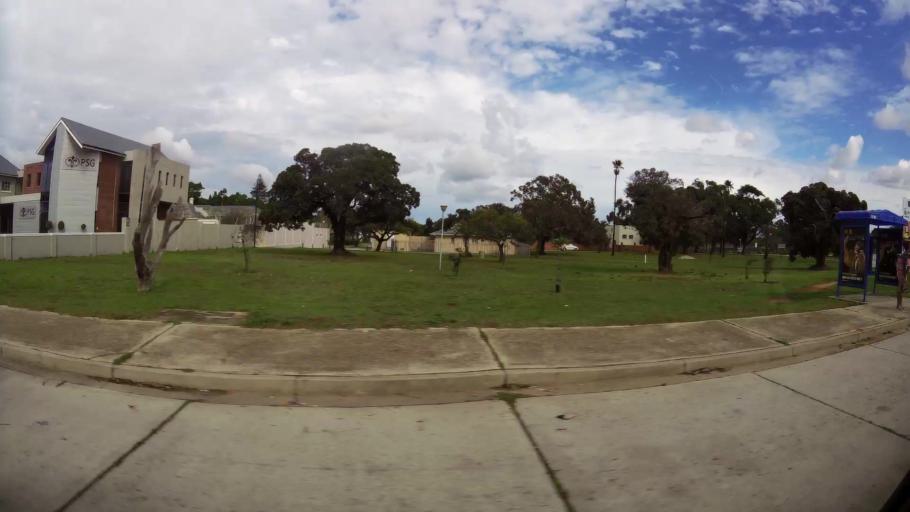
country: ZA
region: Eastern Cape
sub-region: Nelson Mandela Bay Metropolitan Municipality
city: Port Elizabeth
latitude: -33.9572
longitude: 25.5917
